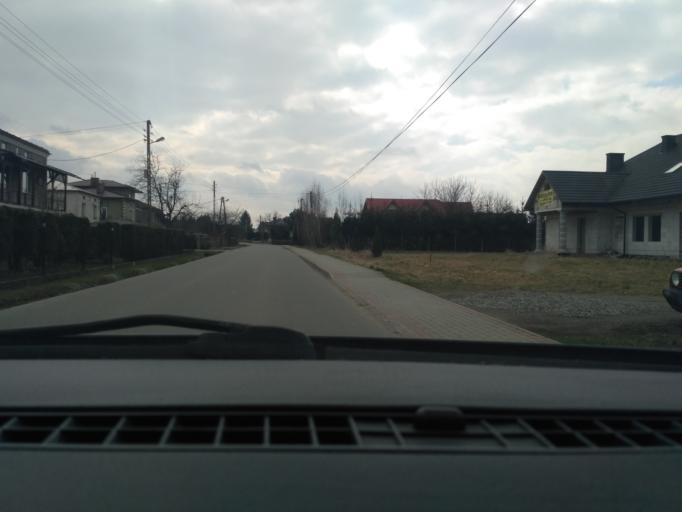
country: PL
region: Subcarpathian Voivodeship
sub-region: Powiat krosnienski
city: Kroscienko Wyzne
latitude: 49.6638
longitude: 21.8314
